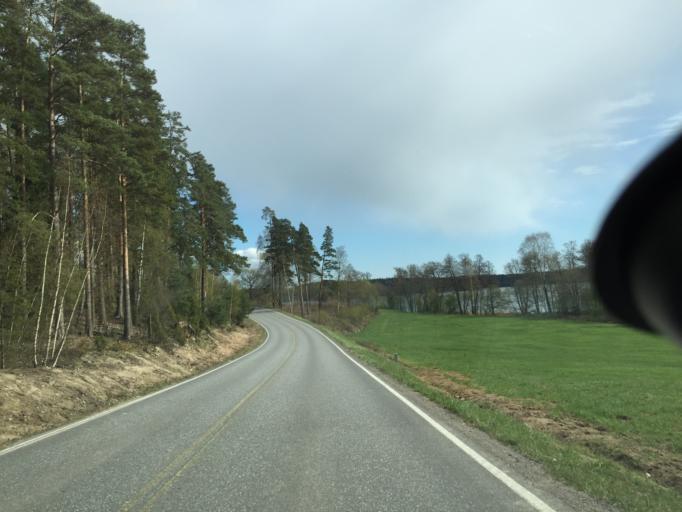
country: FI
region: Varsinais-Suomi
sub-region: Salo
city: Pernioe
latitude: 60.0329
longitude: 23.1930
